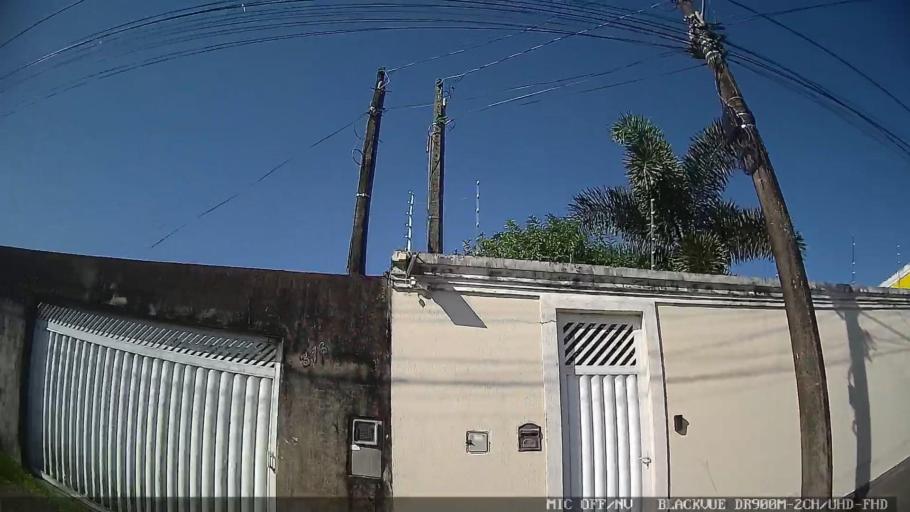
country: BR
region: Sao Paulo
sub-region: Guaruja
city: Guaruja
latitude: -23.9714
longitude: -46.2116
